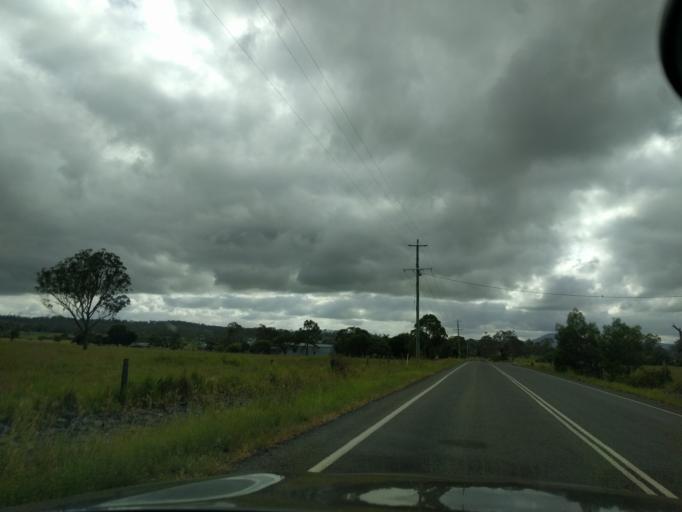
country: AU
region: Queensland
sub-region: Logan
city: Cedar Vale
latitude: -28.0206
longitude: 152.9954
